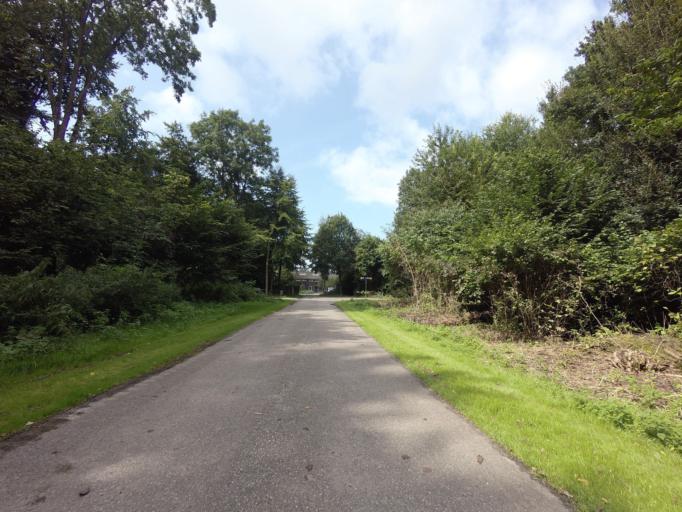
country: NL
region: Flevoland
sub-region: Gemeente Lelystad
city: Lelystad
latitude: 52.4814
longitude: 5.5243
